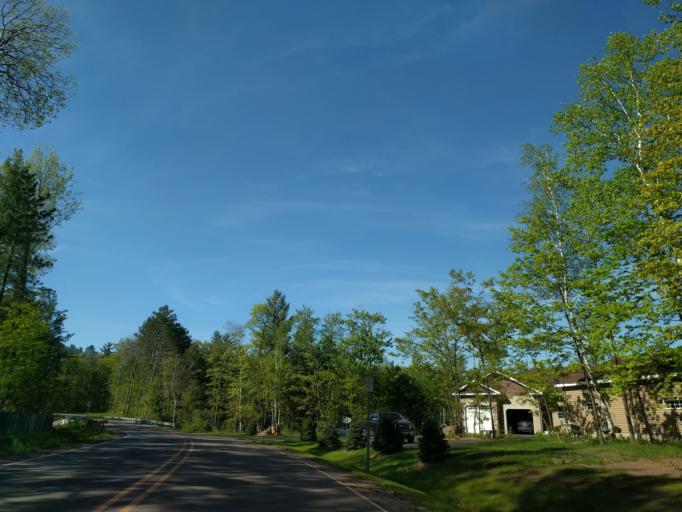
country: US
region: Michigan
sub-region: Marquette County
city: Gwinn
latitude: 46.2723
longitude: -87.3688
